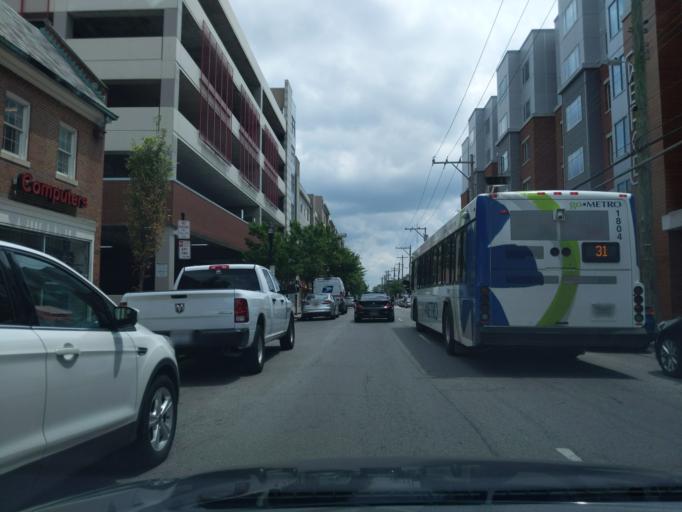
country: US
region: Kentucky
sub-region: Campbell County
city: Newport
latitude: 39.1278
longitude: -84.5190
